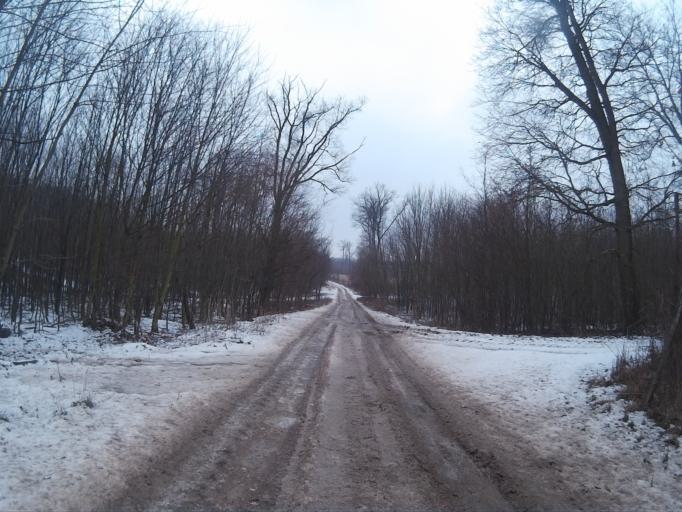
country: HU
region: Komarom-Esztergom
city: Tarjan
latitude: 47.5751
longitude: 18.5239
